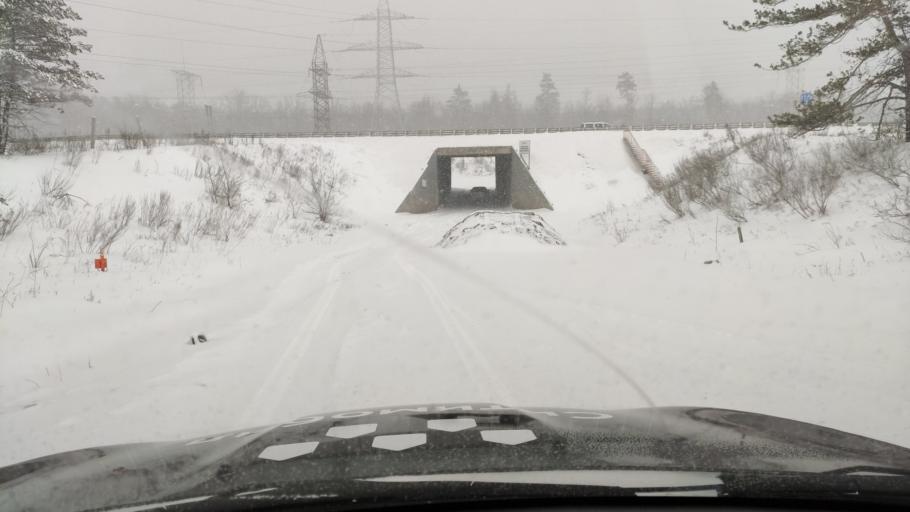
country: RU
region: Samara
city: Povolzhskiy
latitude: 53.5163
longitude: 49.6854
